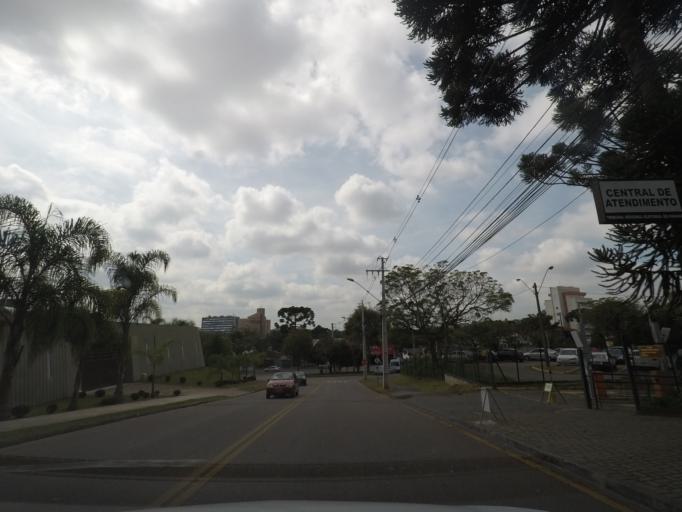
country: BR
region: Parana
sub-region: Curitiba
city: Curitiba
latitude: -25.4561
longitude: -49.2557
